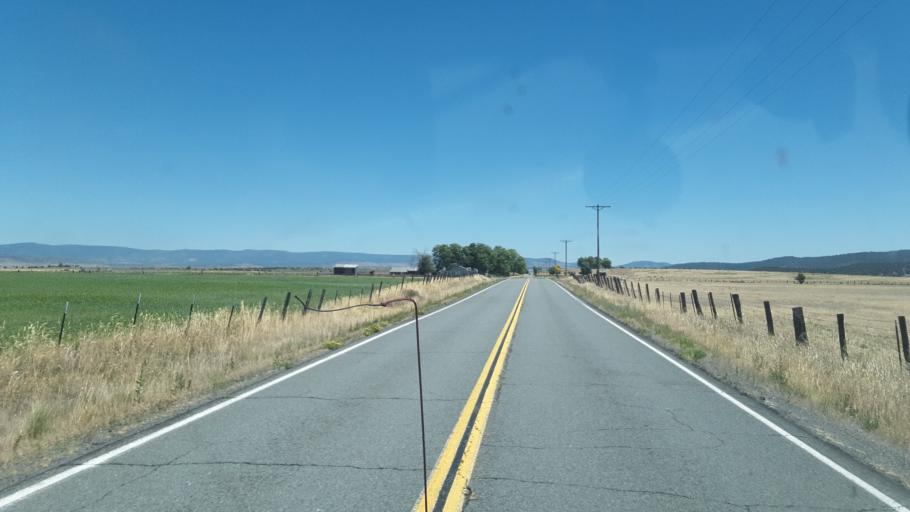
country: US
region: California
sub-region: Shasta County
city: Burney
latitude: 41.1320
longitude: -121.1004
